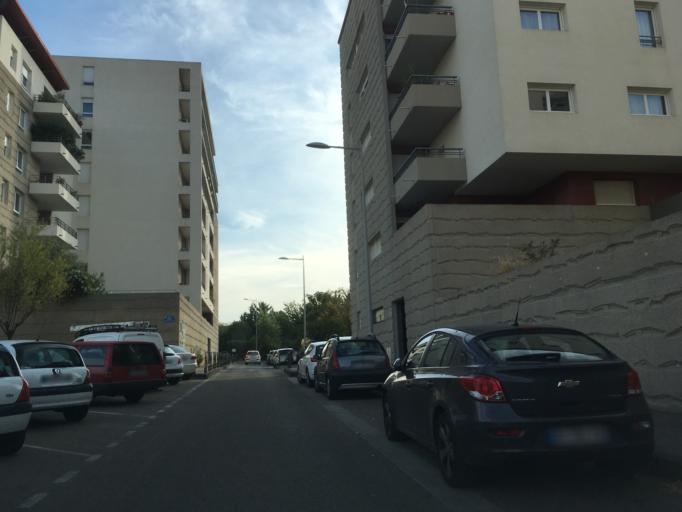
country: FR
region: Languedoc-Roussillon
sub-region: Departement de l'Herault
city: Castelnau-le-Lez
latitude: 43.6059
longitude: 3.9101
